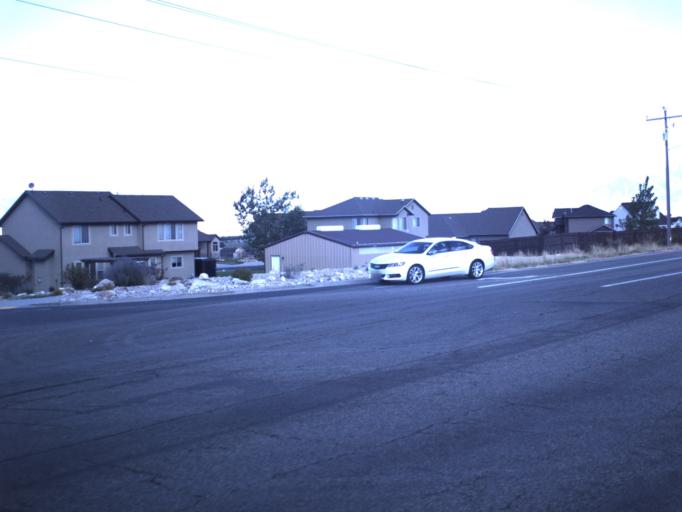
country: US
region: Utah
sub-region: Tooele County
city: Grantsville
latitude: 40.6195
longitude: -112.5021
